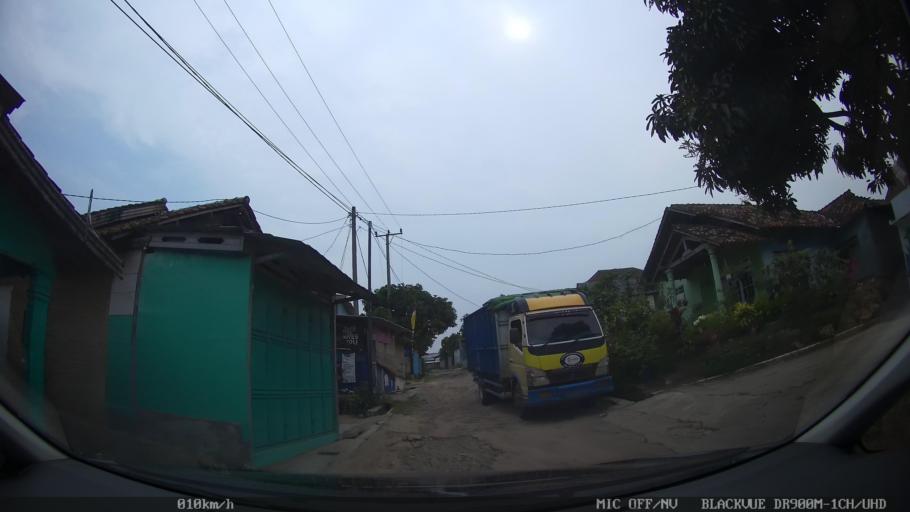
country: ID
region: Lampung
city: Panjang
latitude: -5.4337
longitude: 105.3331
